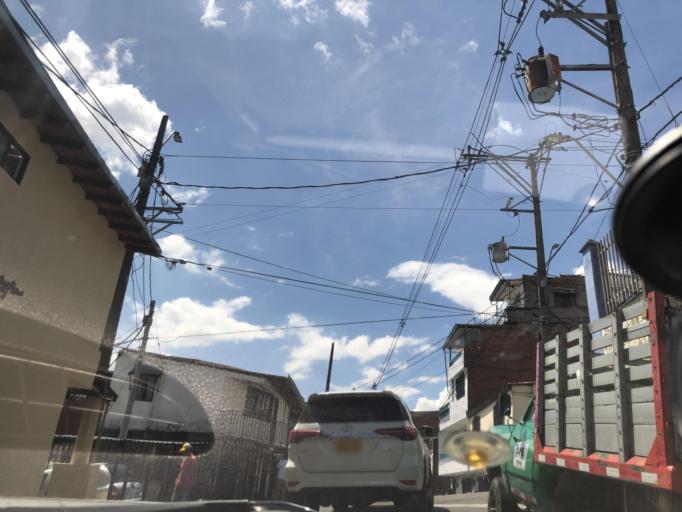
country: CO
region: Antioquia
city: Bello
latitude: 6.3113
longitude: -75.5812
